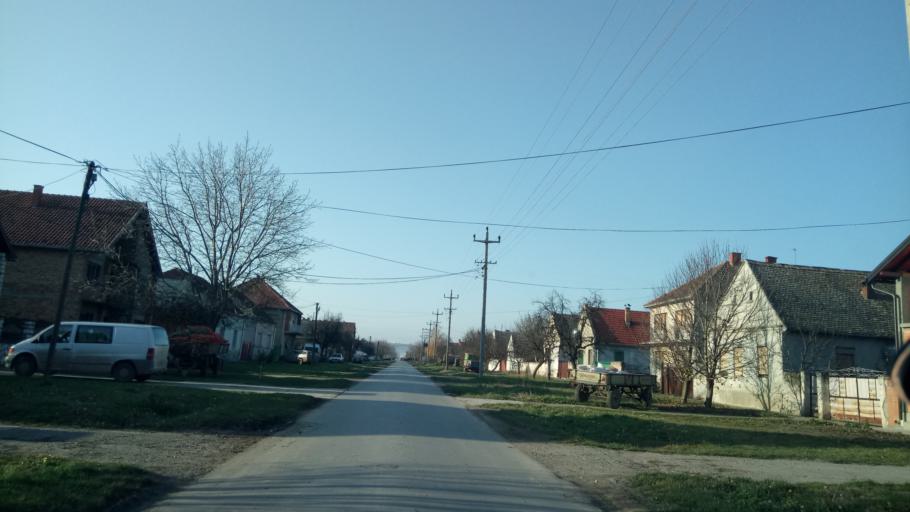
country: RS
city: Novi Slankamen
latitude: 45.1290
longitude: 20.2384
